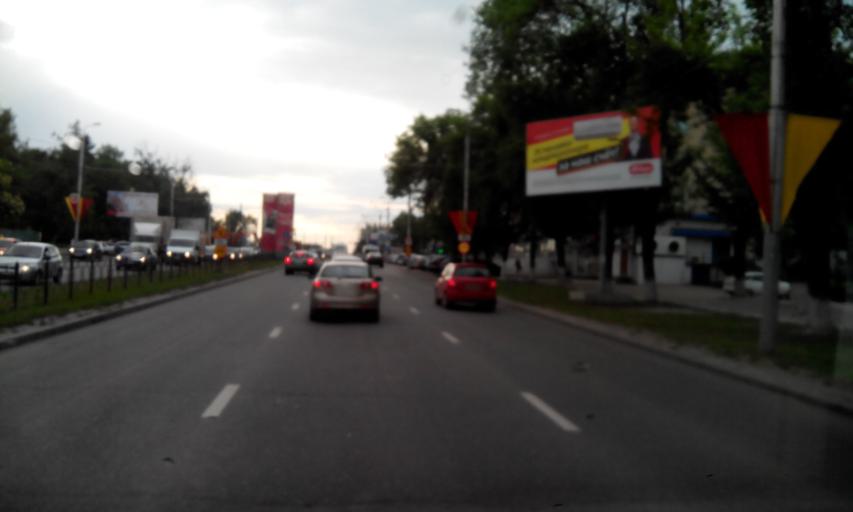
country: RU
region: Penza
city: Penza
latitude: 53.2161
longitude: 44.9832
